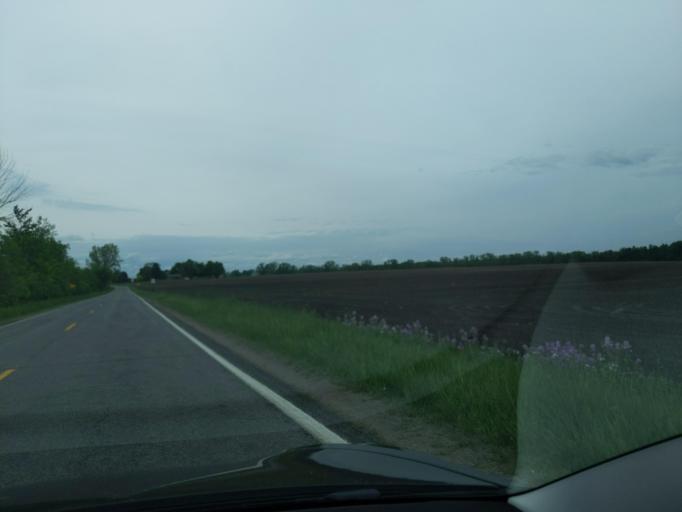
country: US
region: Michigan
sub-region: Ingham County
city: Mason
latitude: 42.5396
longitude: -84.4231
